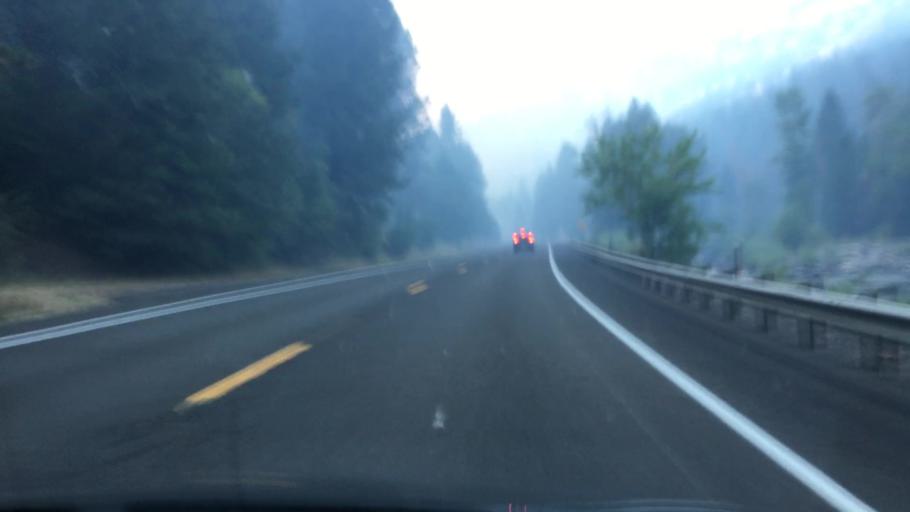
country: US
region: Idaho
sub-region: Valley County
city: McCall
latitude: 45.2420
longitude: -116.3319
